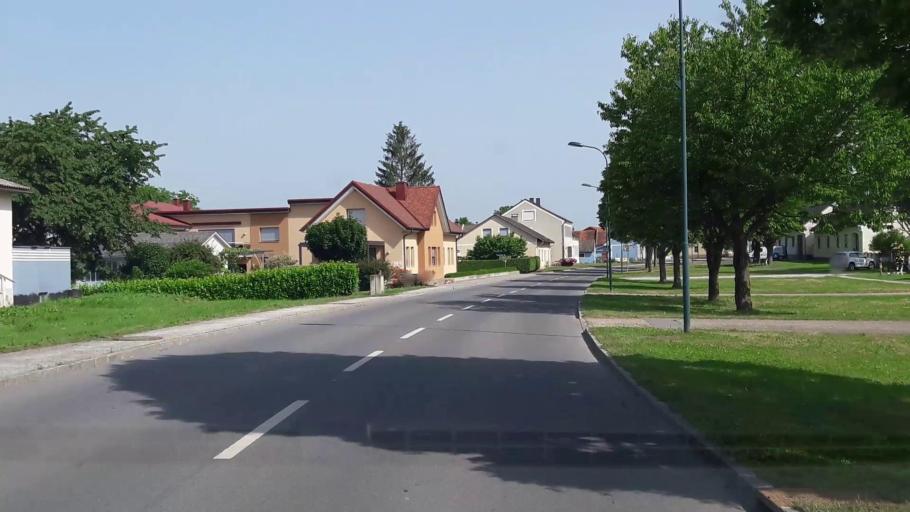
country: AT
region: Burgenland
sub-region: Politischer Bezirk Jennersdorf
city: Deutsch Kaltenbrunn
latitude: 47.0852
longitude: 16.1066
